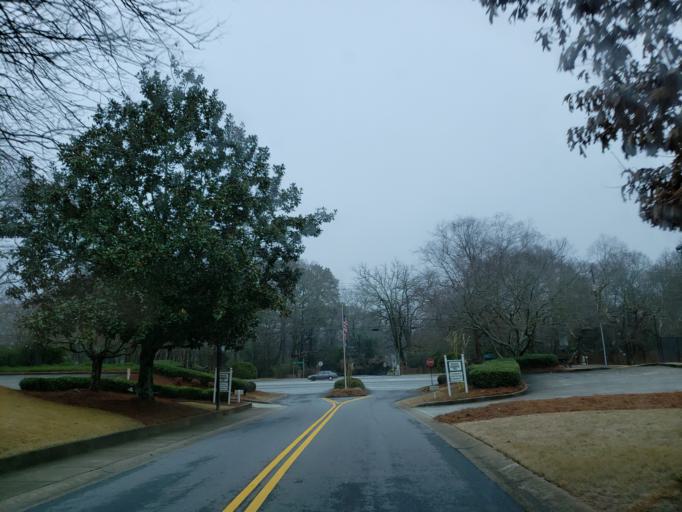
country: US
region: Georgia
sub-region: Cobb County
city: Fair Oaks
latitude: 33.9280
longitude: -84.5707
